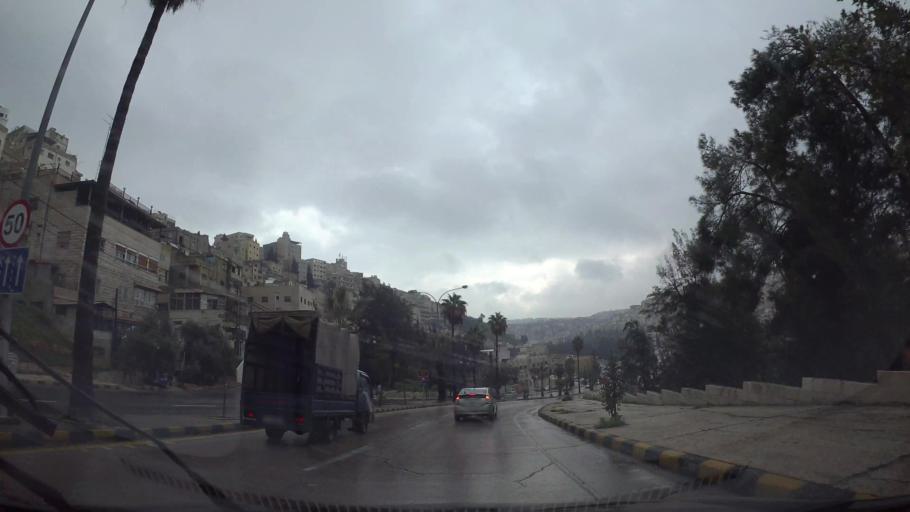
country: JO
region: Amman
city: Amman
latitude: 31.9495
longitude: 35.9142
